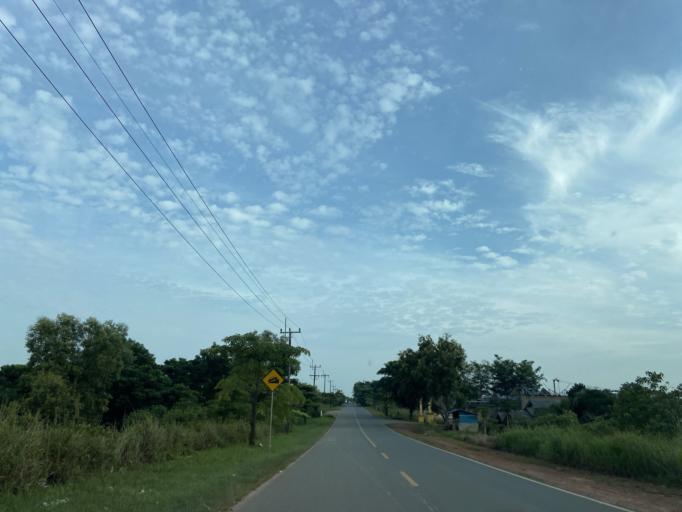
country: ID
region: Riau Islands
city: Tanjungpinang
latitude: 0.9224
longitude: 104.1170
